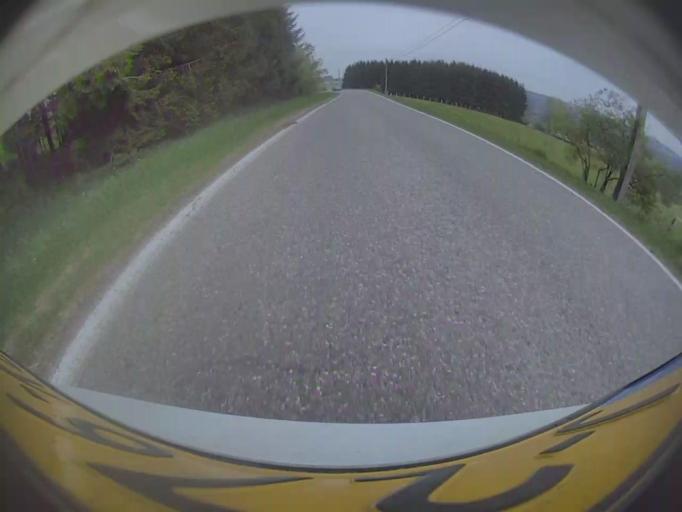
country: BE
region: Wallonia
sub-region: Province du Luxembourg
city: La Roche-en-Ardenne
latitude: 50.2266
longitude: 5.6237
